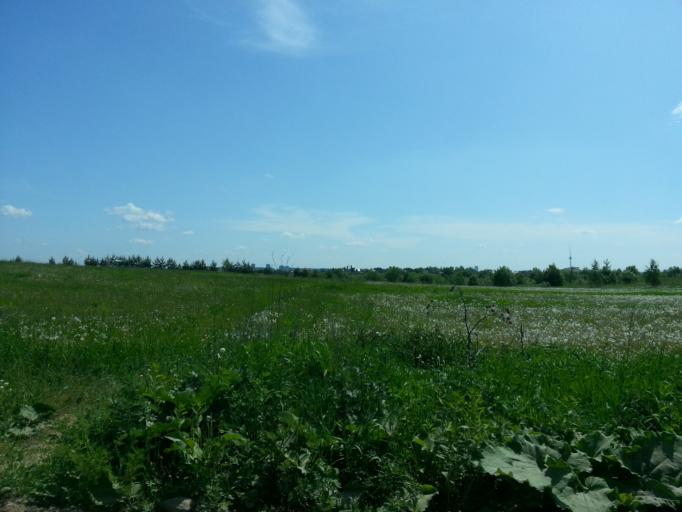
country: LT
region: Vilnius County
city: Pilaite
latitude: 54.7354
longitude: 25.1583
